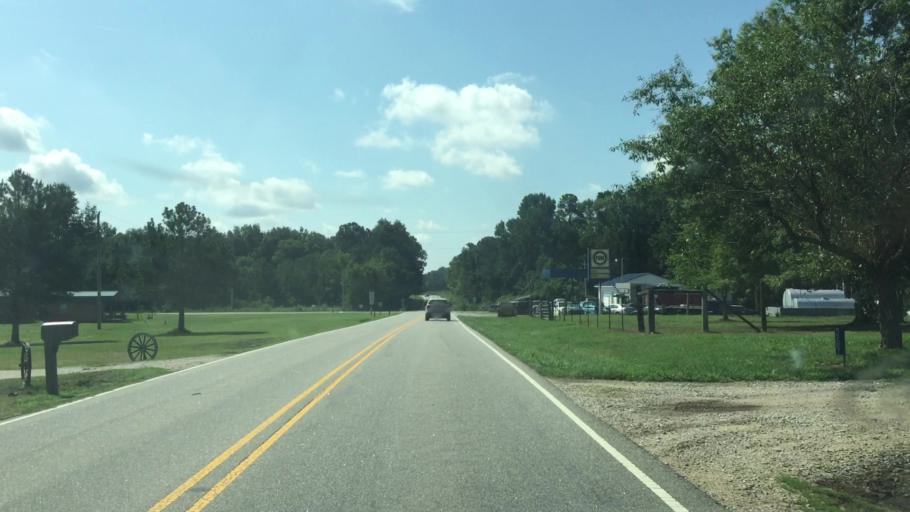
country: US
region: North Carolina
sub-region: Anson County
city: Burnsville
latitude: 35.0538
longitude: -80.2712
